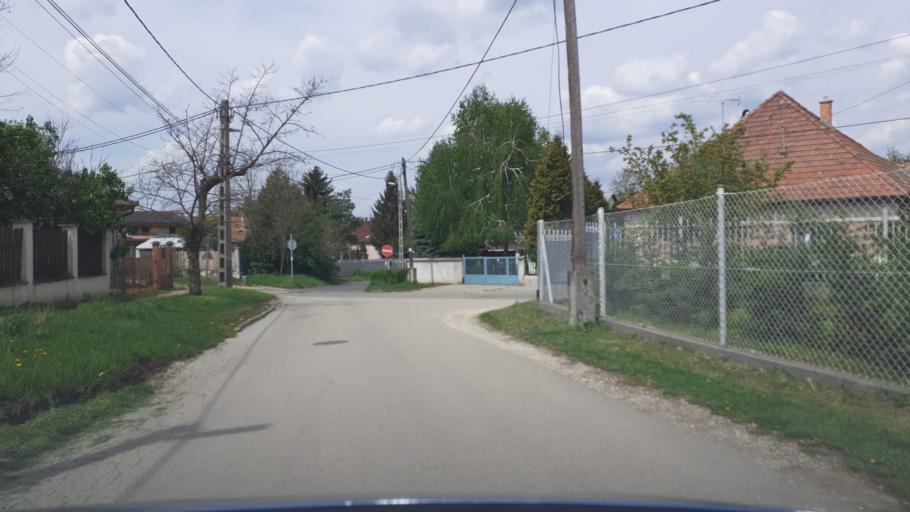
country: HU
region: Pest
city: Pecel
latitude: 47.4766
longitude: 19.3469
